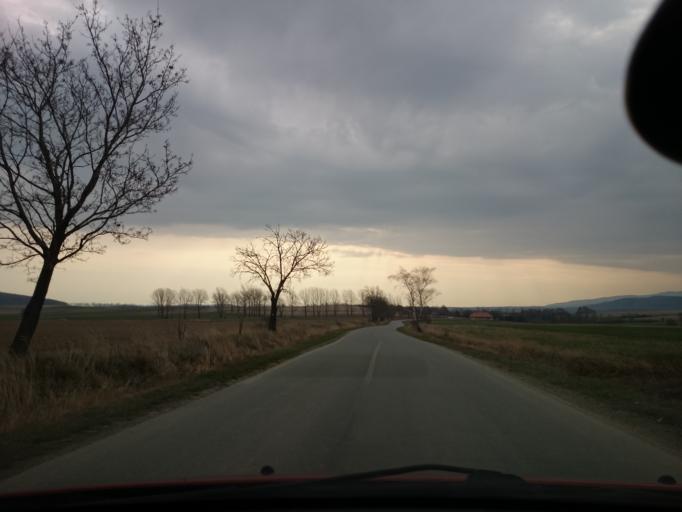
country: PL
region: Lower Silesian Voivodeship
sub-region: Powiat zabkowicki
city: Bardo
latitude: 50.5351
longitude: 16.7363
